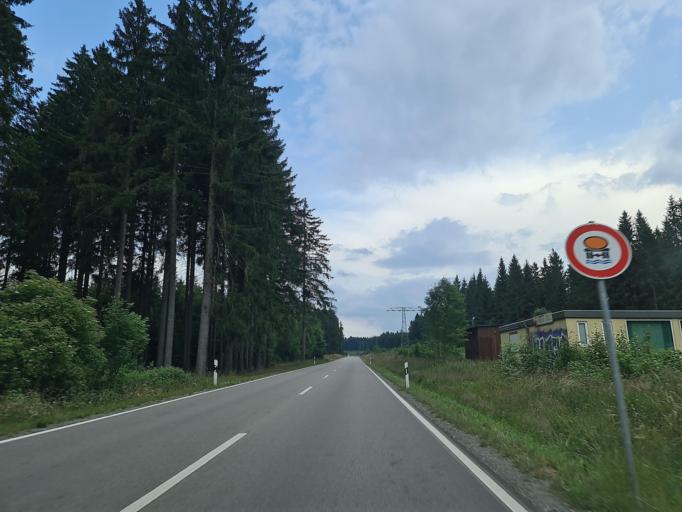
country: DE
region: Saxony
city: Grunbach
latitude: 50.4369
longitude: 12.3655
